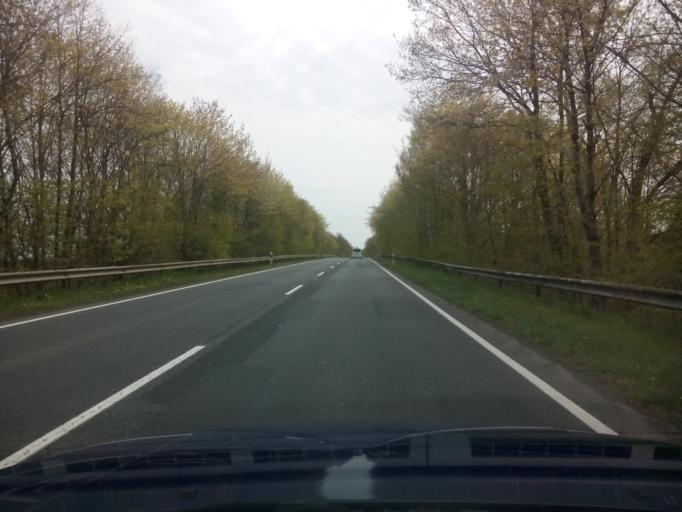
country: DE
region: Lower Saxony
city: Syke
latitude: 52.9499
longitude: 8.8177
